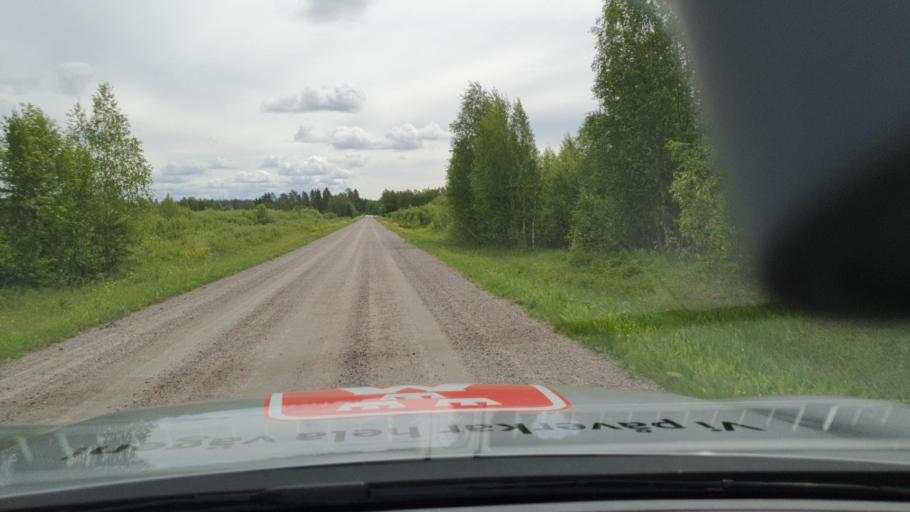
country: SE
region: Norrbotten
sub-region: Haparanda Kommun
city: Haparanda
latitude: 65.9495
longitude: 23.7835
